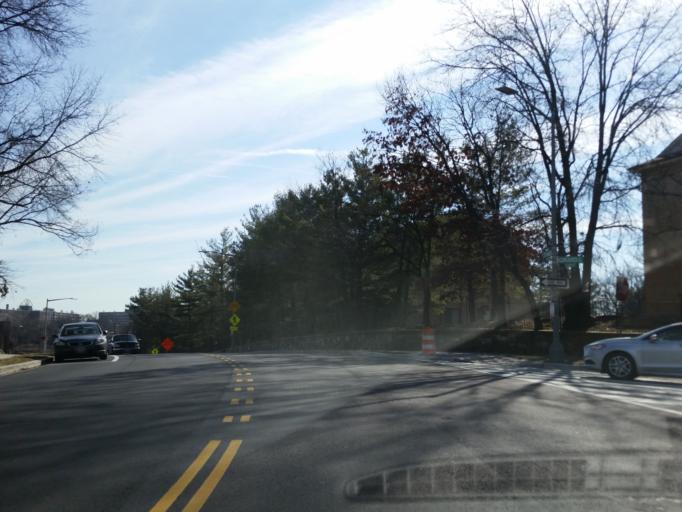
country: US
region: Maryland
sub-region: Prince George's County
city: Chillum
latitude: 38.9263
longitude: -77.0059
